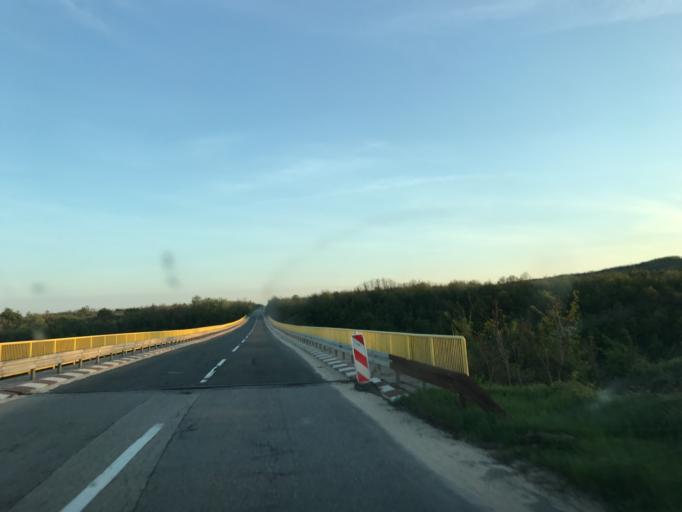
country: RO
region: Mehedinti
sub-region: Comuna Gogosu
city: Ostrovu Mare
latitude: 44.3707
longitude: 22.4803
